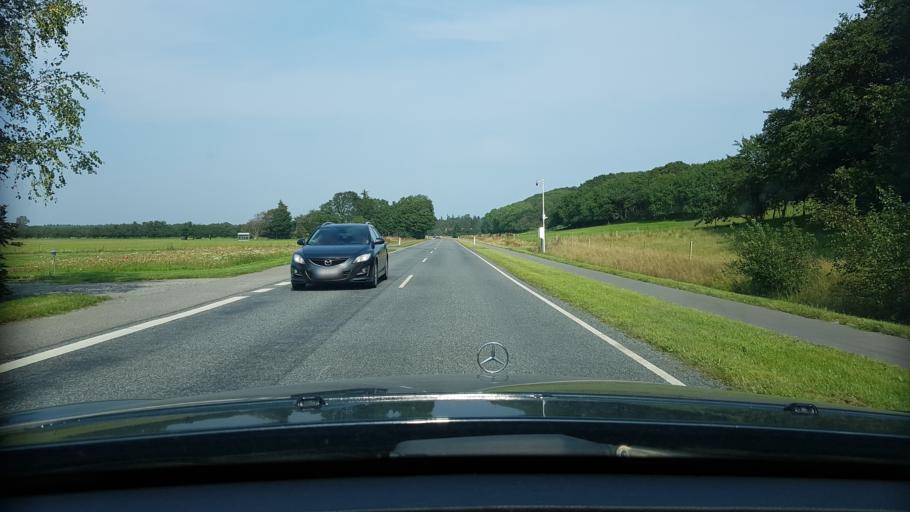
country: DK
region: North Denmark
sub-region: Alborg Kommune
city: Hals
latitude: 56.9141
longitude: 10.2549
